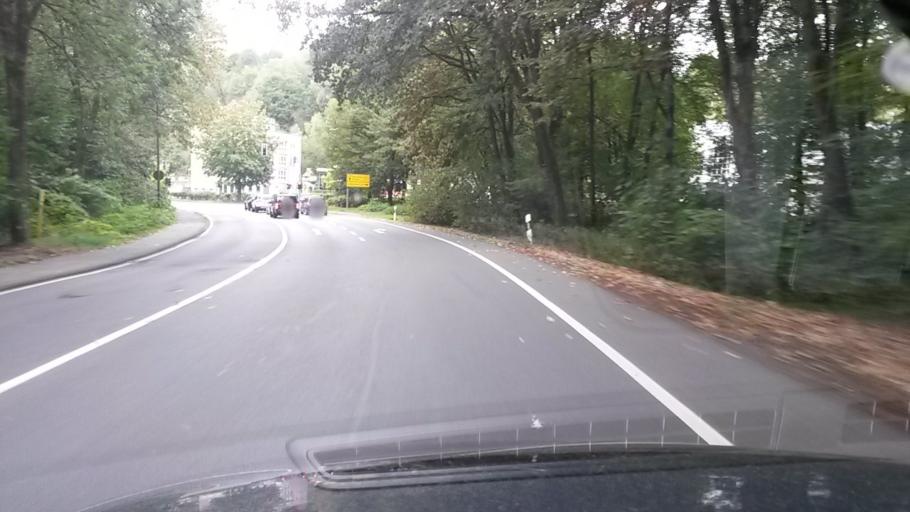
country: DE
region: North Rhine-Westphalia
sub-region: Regierungsbezirk Arnsberg
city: Luedenscheid
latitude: 51.2109
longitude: 7.6176
